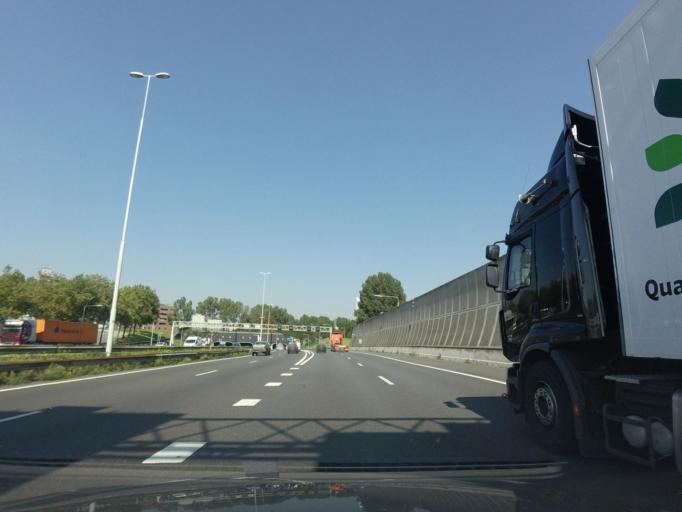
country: NL
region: South Holland
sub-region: Gemeente Zwijndrecht
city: Zwijndrecht
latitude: 51.8047
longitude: 4.6505
